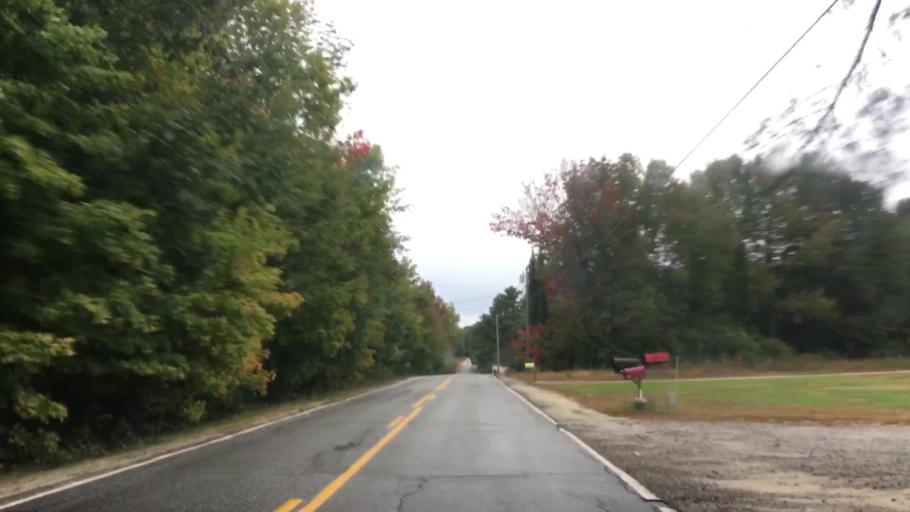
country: US
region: Maine
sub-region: Cumberland County
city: Raymond
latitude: 43.9700
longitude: -70.4679
